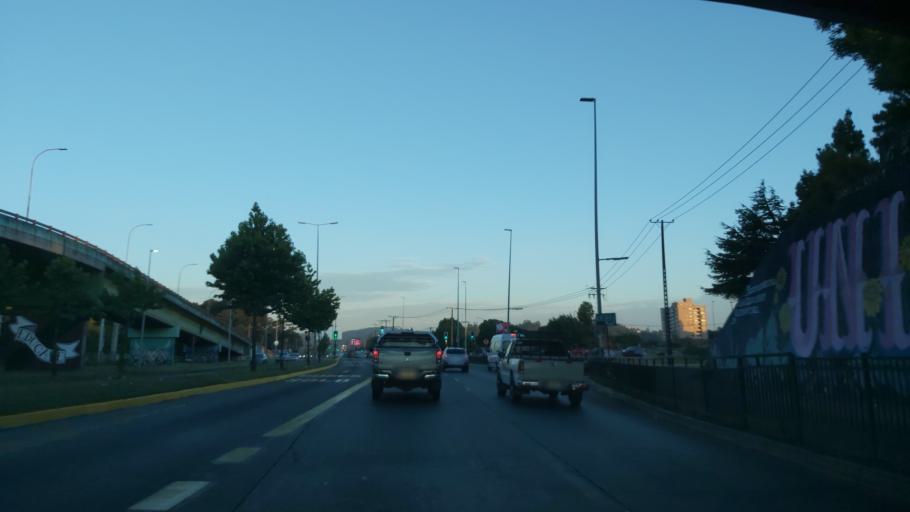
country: CL
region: Biobio
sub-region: Provincia de Concepcion
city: Concepcion
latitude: -36.8387
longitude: -73.1009
